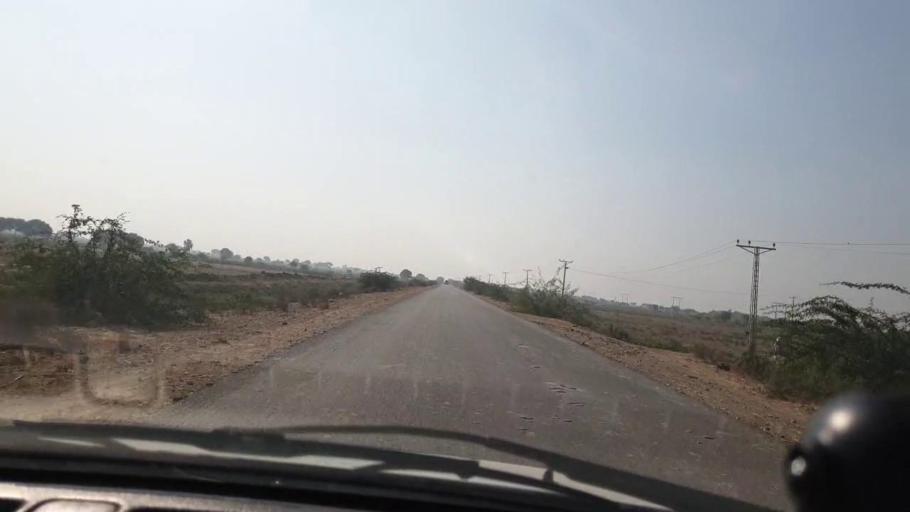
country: PK
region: Sindh
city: Bulri
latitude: 24.9157
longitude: 68.3493
